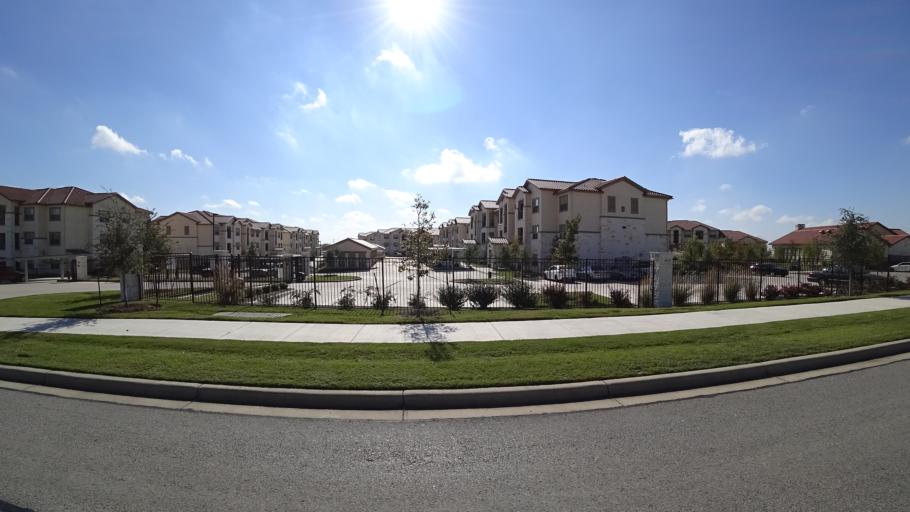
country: US
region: Texas
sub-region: Travis County
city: Windemere
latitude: 30.4332
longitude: -97.6515
